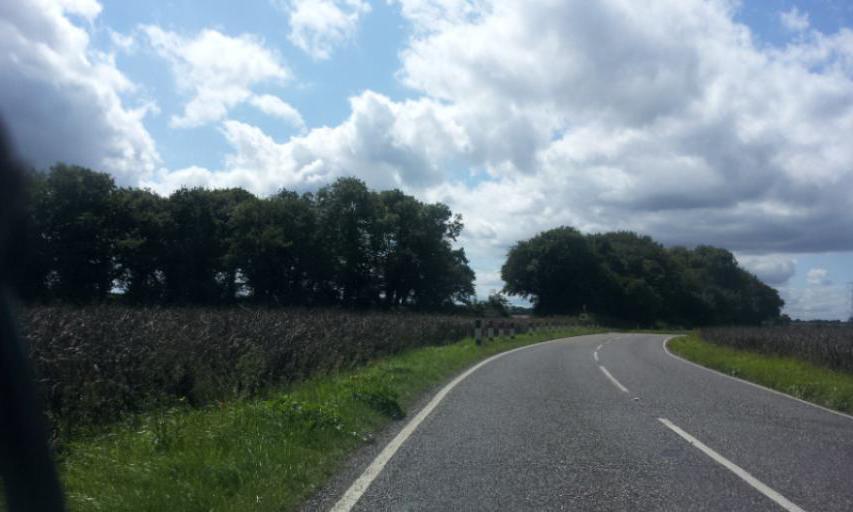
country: GB
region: England
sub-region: Kent
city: Boxley
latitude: 51.3227
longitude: 0.5597
